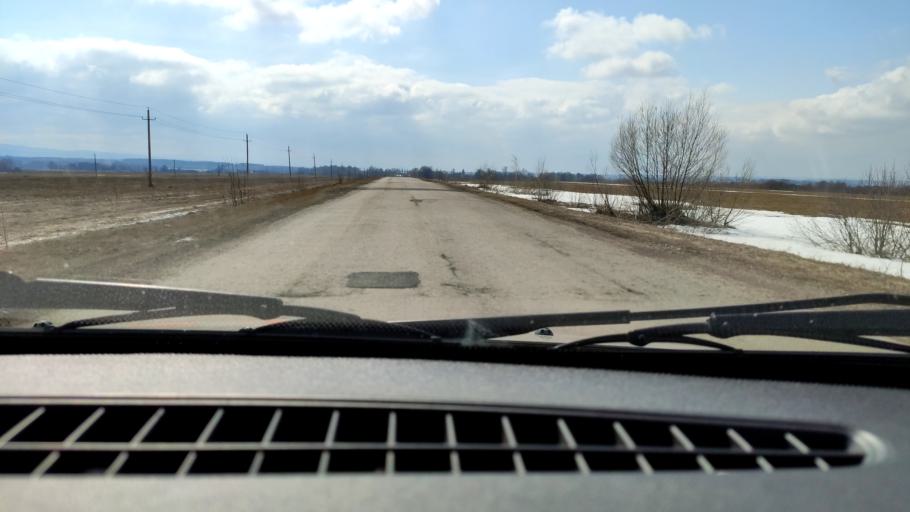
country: RU
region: Bashkortostan
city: Kudeyevskiy
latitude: 54.8418
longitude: 56.7957
